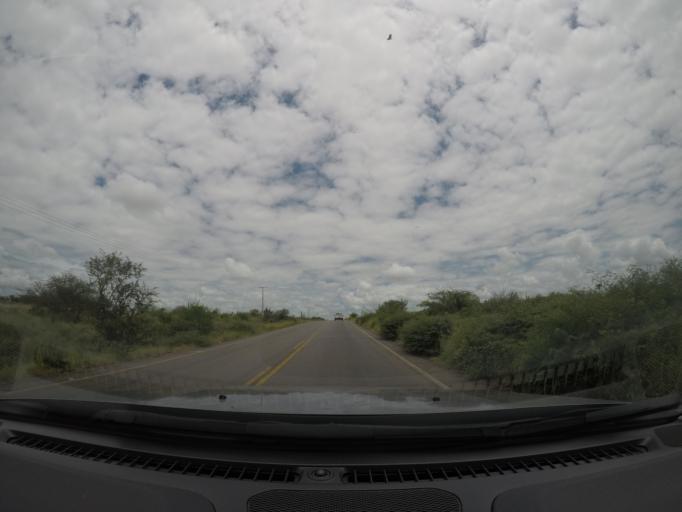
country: BR
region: Bahia
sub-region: Itaberaba
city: Itaberaba
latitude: -12.4784
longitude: -40.2046
